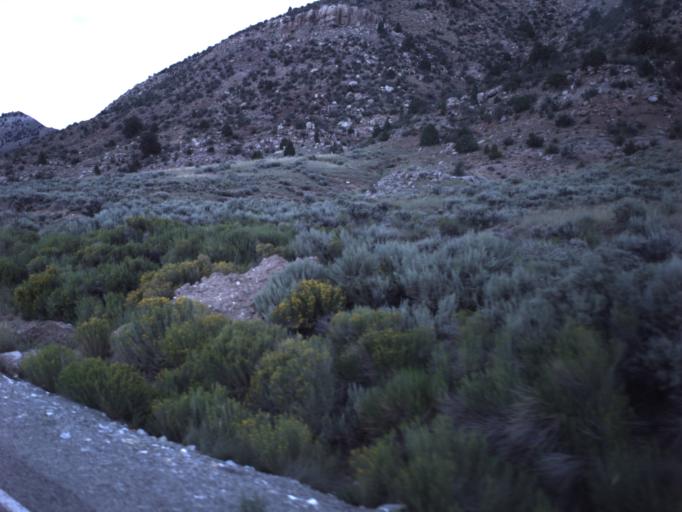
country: US
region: Utah
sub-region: Carbon County
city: Helper
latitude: 39.8241
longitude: -110.7860
